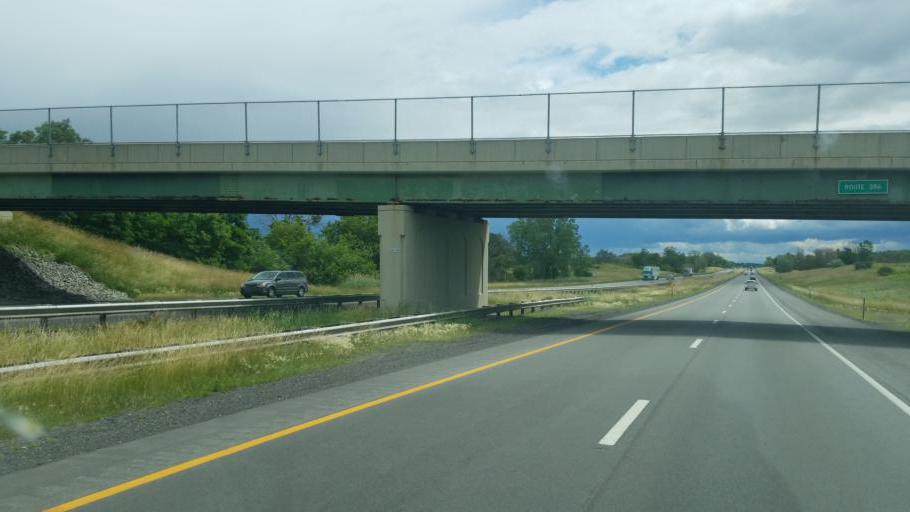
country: US
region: New York
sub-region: Monroe County
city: Scottsville
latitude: 43.0442
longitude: -77.7798
